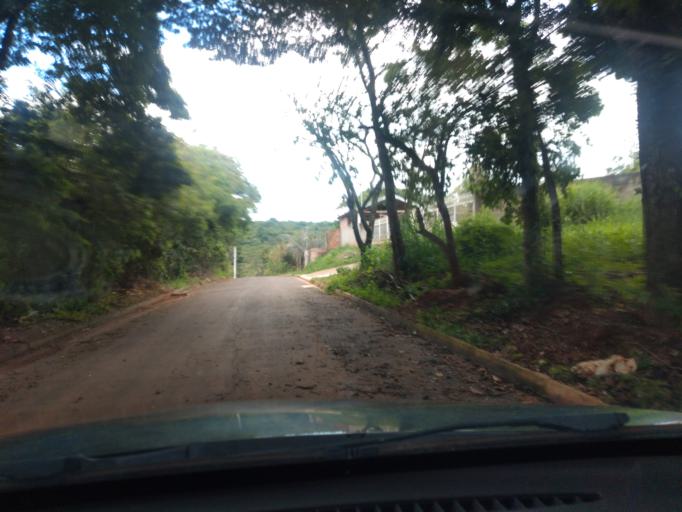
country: BR
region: Minas Gerais
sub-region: Tres Coracoes
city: Tres Coracoes
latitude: -21.6886
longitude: -45.2710
